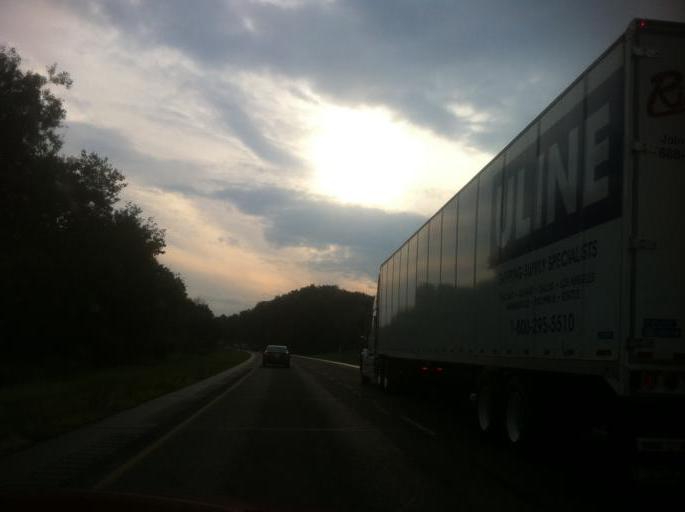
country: US
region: Pennsylvania
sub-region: Clarion County
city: Knox
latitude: 41.1954
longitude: -79.5790
